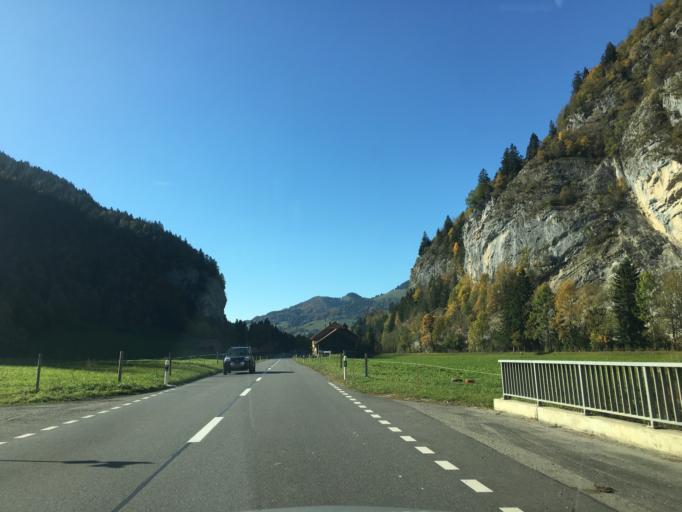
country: CH
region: Fribourg
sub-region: Gruyere District
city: Charmey
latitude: 46.6090
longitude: 7.1881
